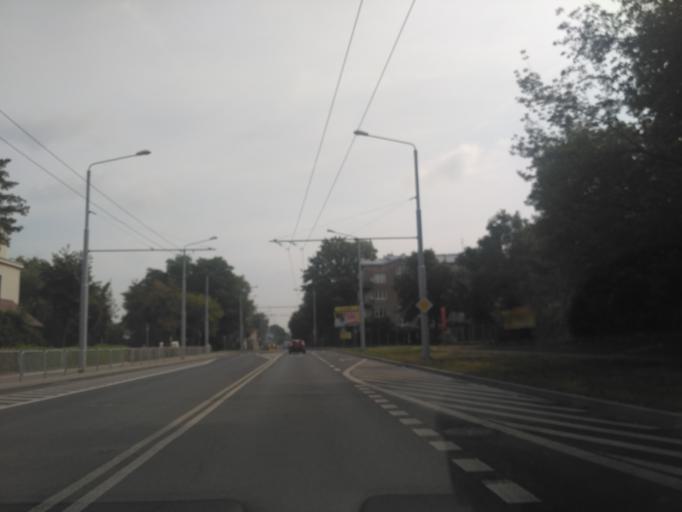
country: PL
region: Lublin Voivodeship
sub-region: Powiat lubelski
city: Lublin
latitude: 51.2236
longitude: 22.5464
